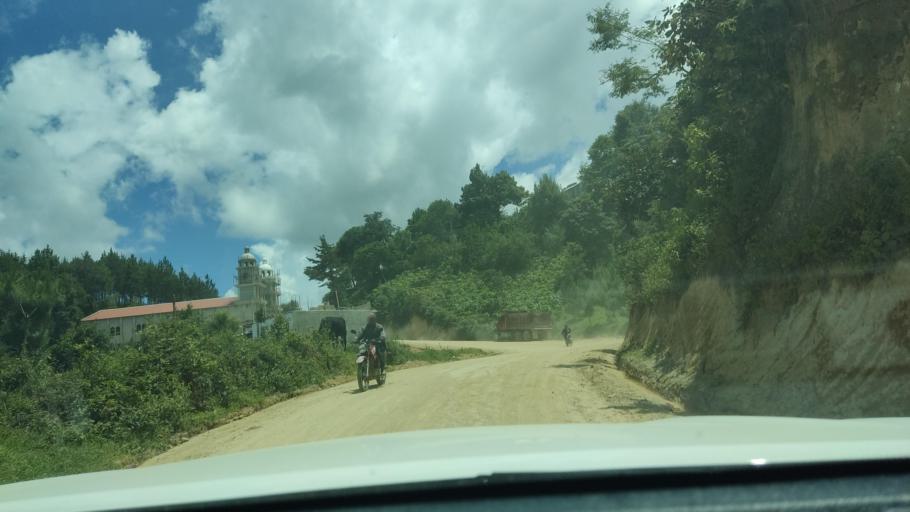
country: GT
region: Chimaltenango
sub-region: Municipio de San Juan Comalapa
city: Comalapa
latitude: 14.7777
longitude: -90.8761
